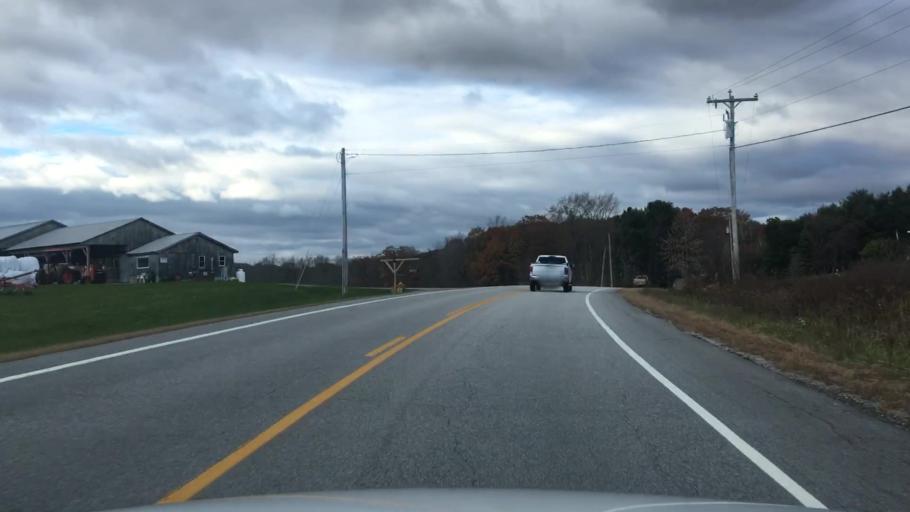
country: US
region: Maine
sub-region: Androscoggin County
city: Leeds
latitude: 44.3369
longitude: -70.1315
